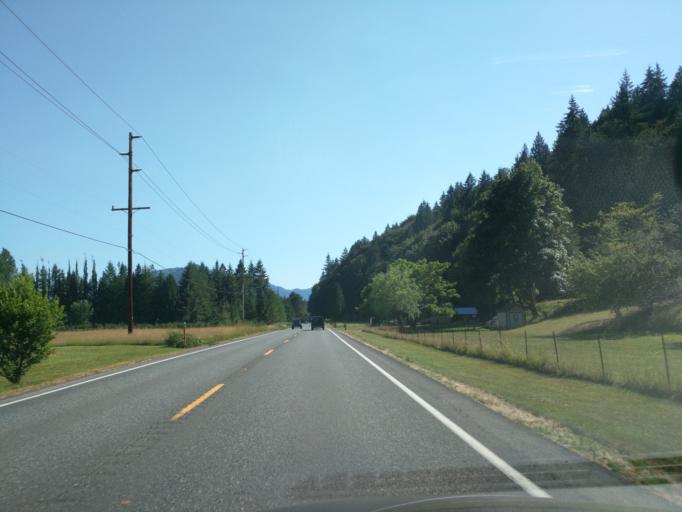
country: US
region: Washington
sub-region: Whatcom County
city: Peaceful Valley
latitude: 48.8579
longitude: -122.1543
